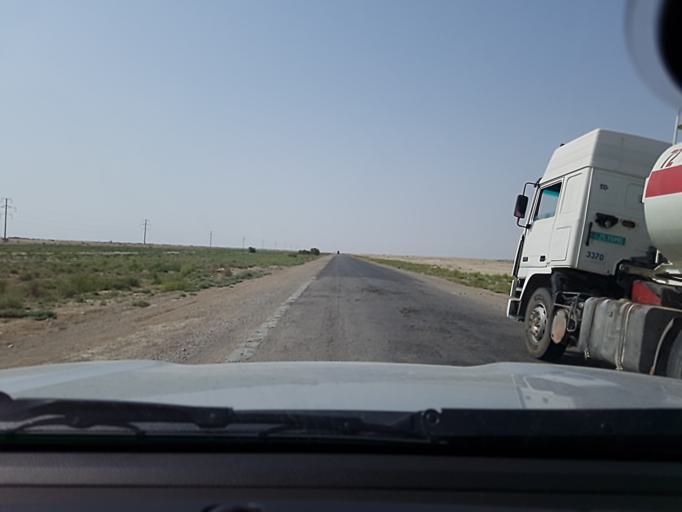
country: TM
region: Balkan
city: Gumdag
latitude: 38.8584
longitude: 54.5949
